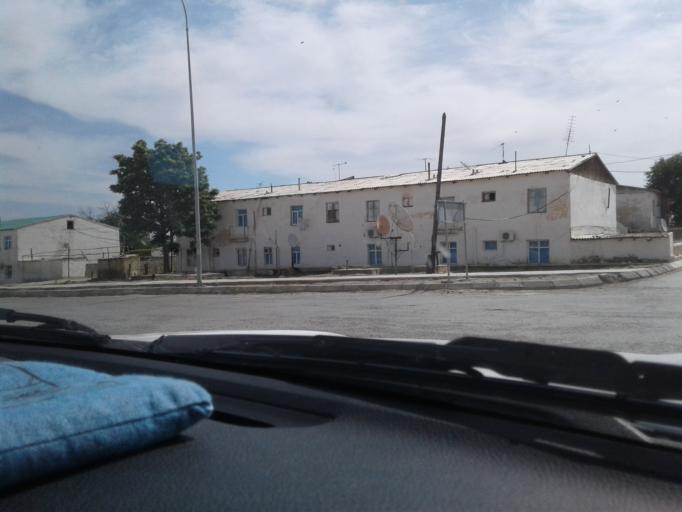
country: TM
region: Balkan
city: Gazanjyk
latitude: 39.2433
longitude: 55.5034
